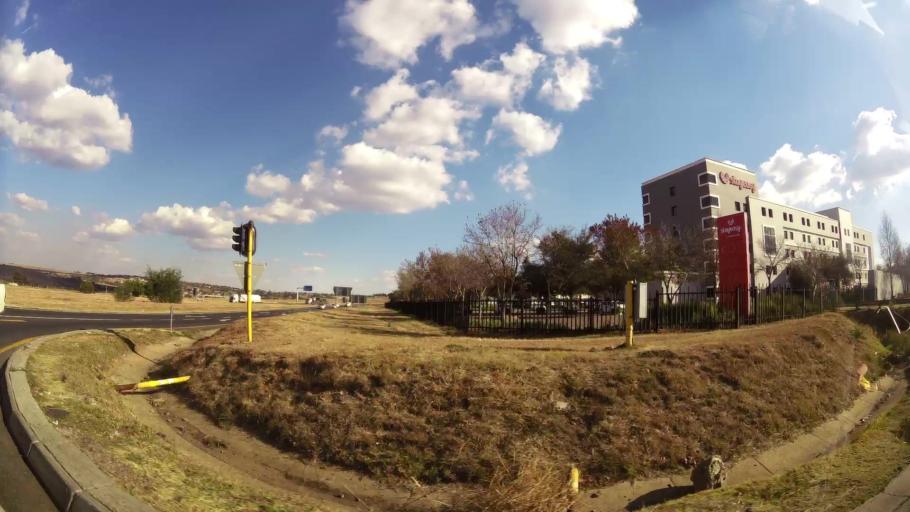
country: ZA
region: Mpumalanga
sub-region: Nkangala District Municipality
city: Witbank
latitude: -25.8870
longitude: 29.2699
